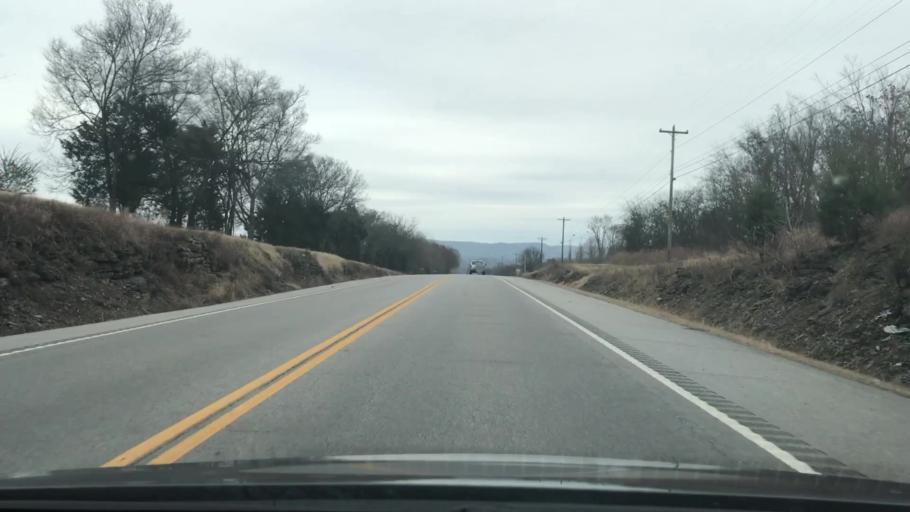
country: US
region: Tennessee
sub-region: Trousdale County
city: Hartsville
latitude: 36.3691
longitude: -86.0937
